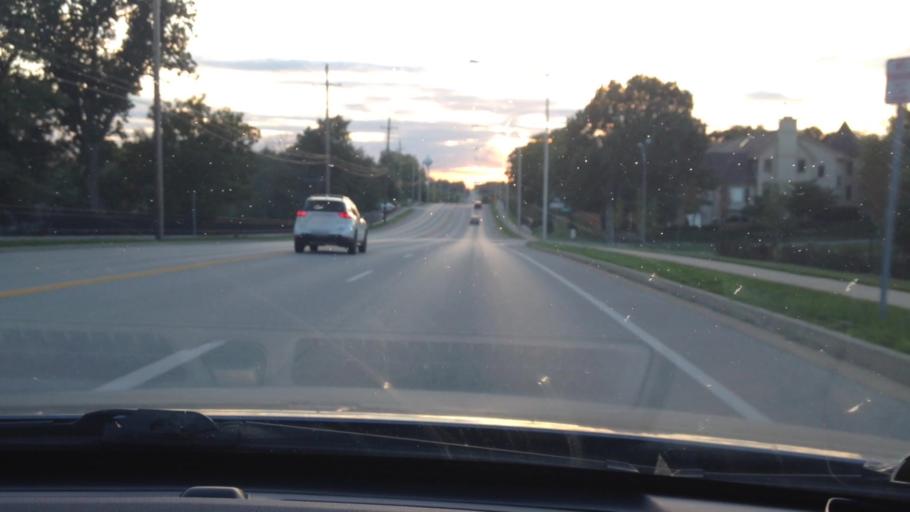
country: US
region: Missouri
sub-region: Platte County
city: Weatherby Lake
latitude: 39.2470
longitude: -94.6794
